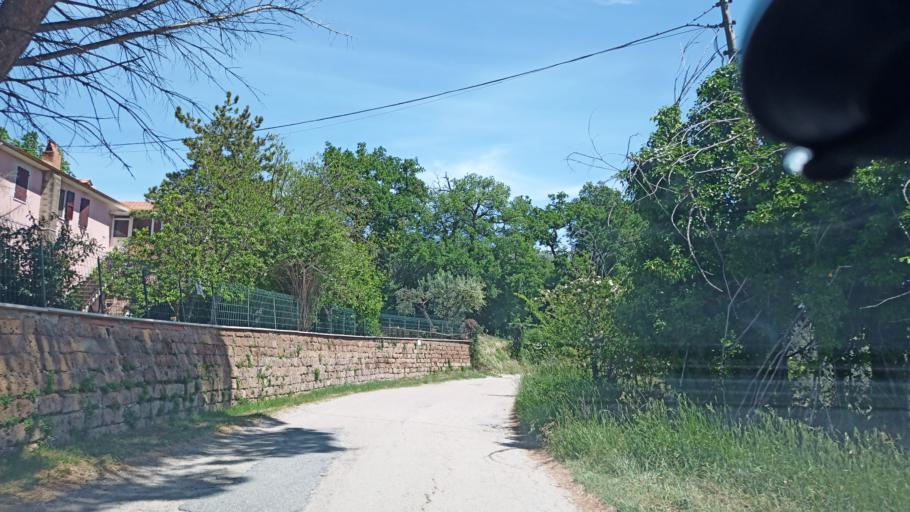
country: IT
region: Latium
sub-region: Provincia di Rieti
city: Torri in Sabina
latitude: 42.3513
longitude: 12.6247
